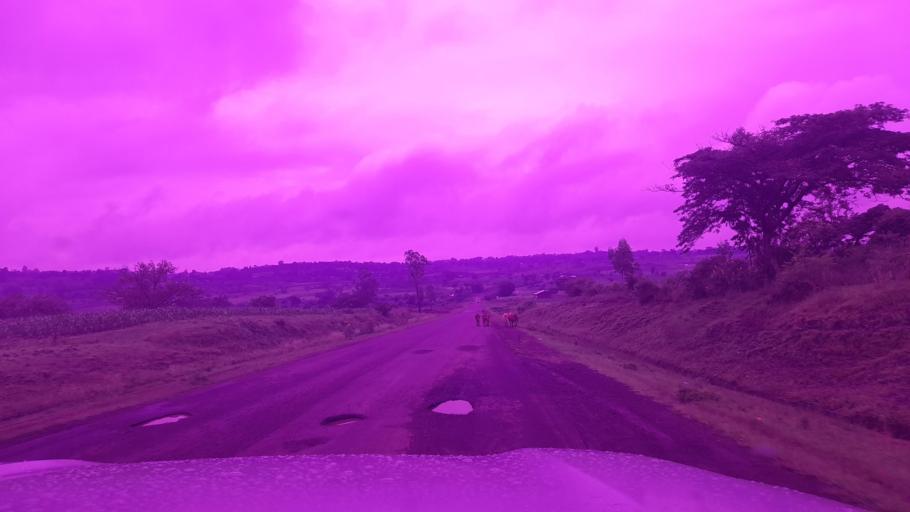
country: ET
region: Oromiya
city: Jima
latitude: 7.6842
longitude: 37.2365
